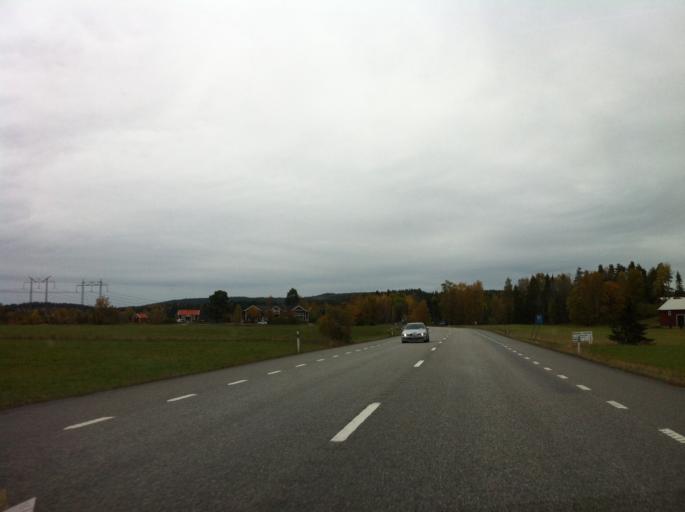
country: SE
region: OErebro
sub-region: Lindesbergs Kommun
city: Stora
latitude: 59.7951
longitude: 15.1535
